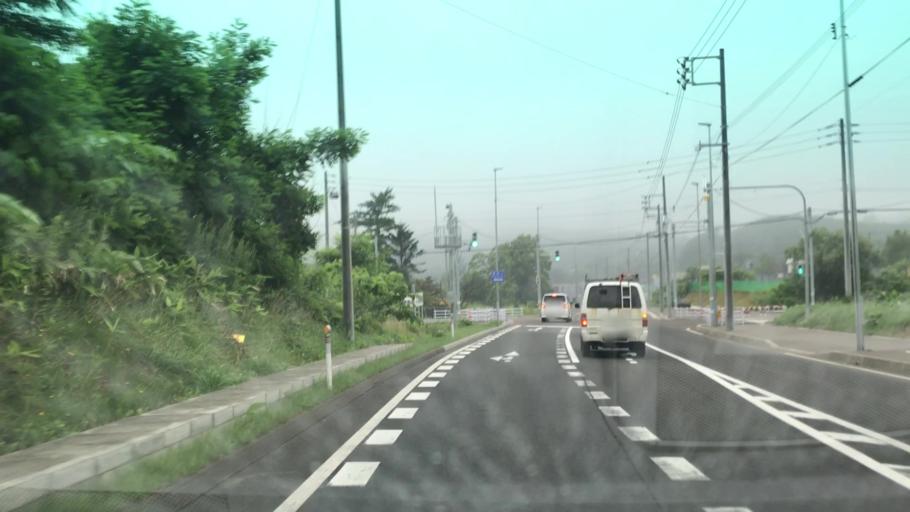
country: JP
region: Hokkaido
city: Sapporo
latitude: 43.0139
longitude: 141.3041
